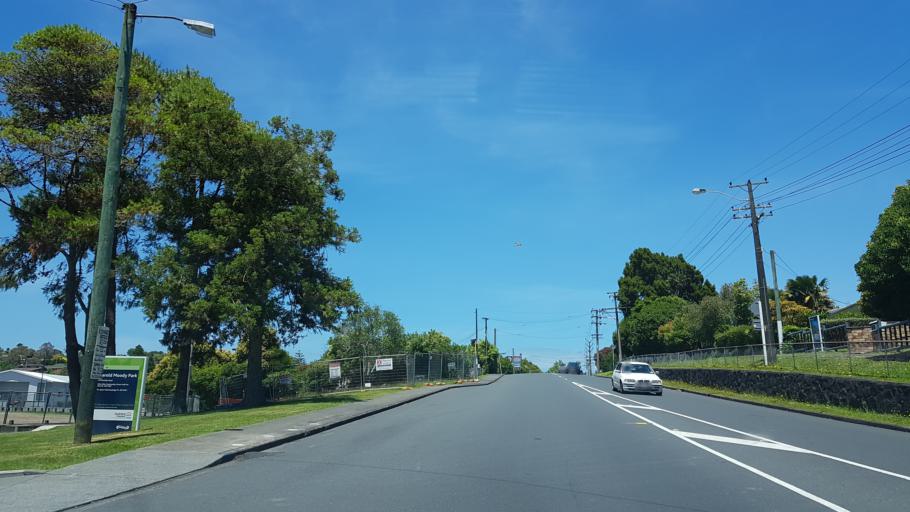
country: NZ
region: Auckland
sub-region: Auckland
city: Waitakere
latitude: -36.9127
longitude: 174.6485
